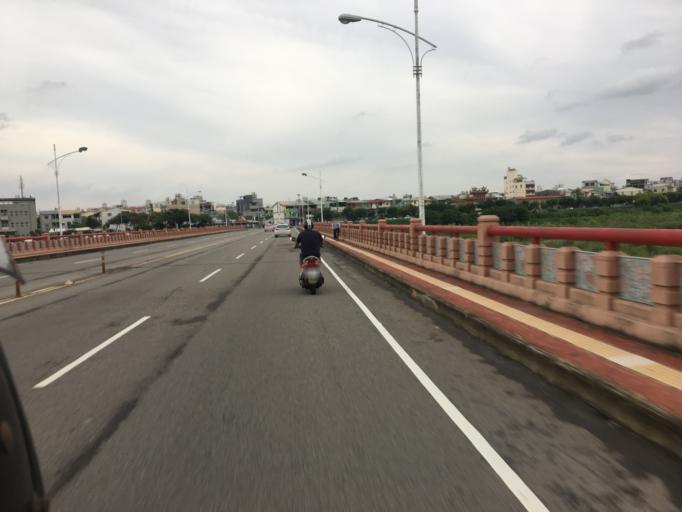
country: TW
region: Taiwan
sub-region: Taichung City
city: Taichung
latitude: 24.1006
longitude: 120.7012
